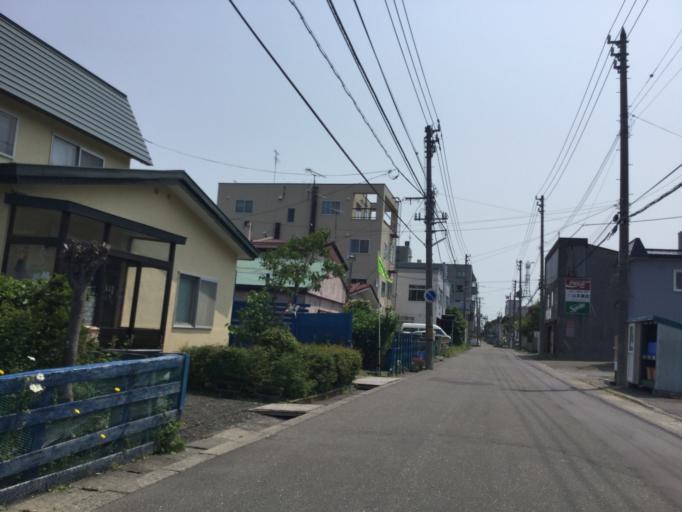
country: JP
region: Hokkaido
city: Wakkanai
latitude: 45.4000
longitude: 141.6780
